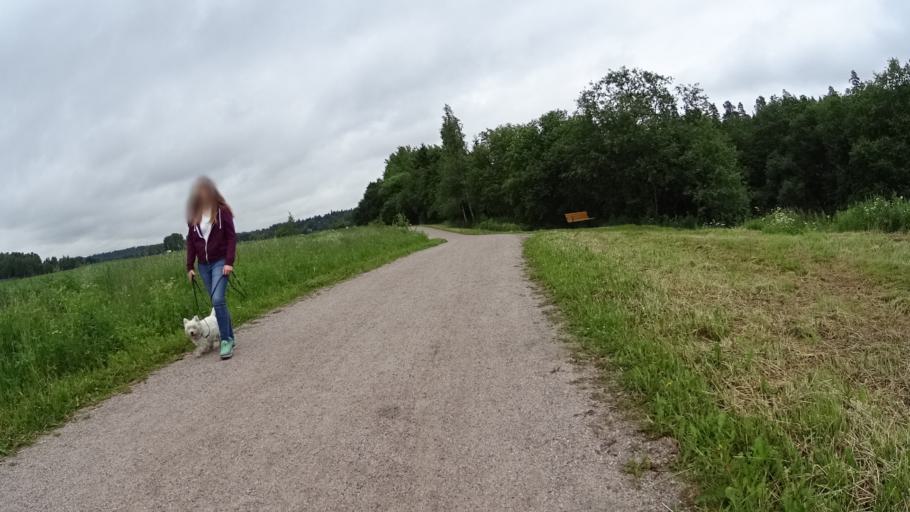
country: FI
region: Uusimaa
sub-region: Helsinki
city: Teekkarikylae
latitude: 60.2829
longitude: 24.8849
